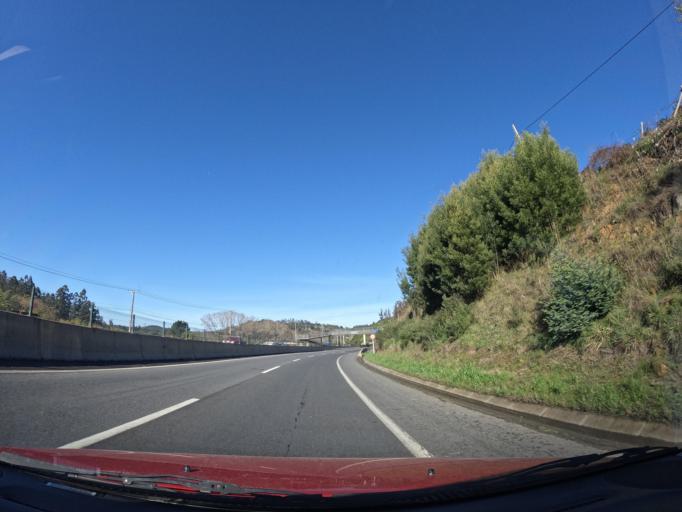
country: CL
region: Biobio
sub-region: Provincia de Concepcion
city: Penco
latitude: -36.8198
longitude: -72.9320
